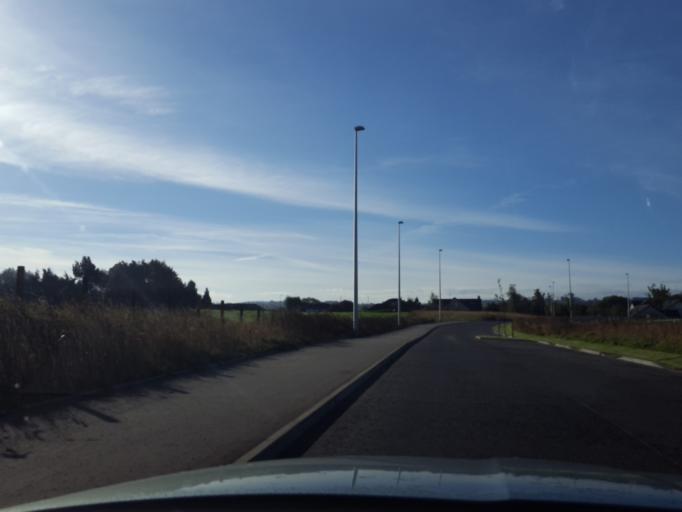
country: GB
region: Scotland
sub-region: West Lothian
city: East Calder
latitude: 55.9000
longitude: -3.4505
